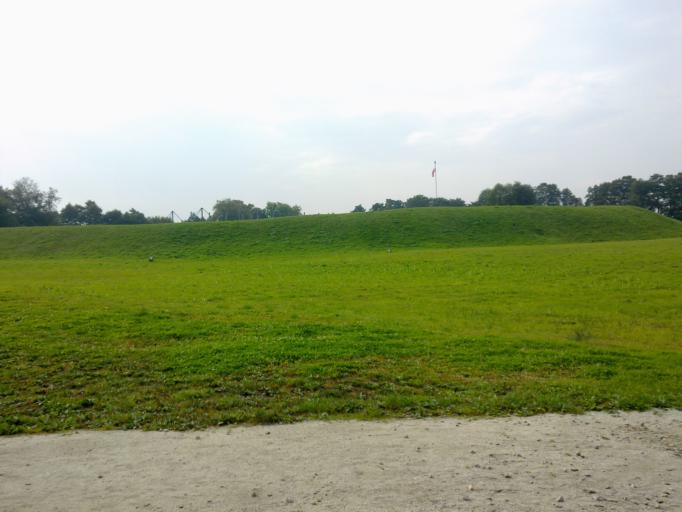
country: PL
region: Greater Poland Voivodeship
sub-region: Powiat gnieznienski
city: Lubowo
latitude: 52.5271
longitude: 17.3786
